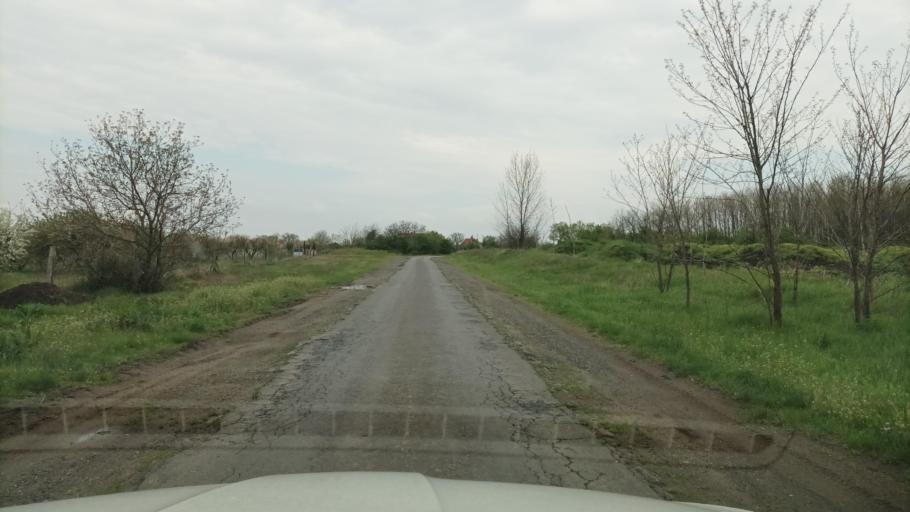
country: HU
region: Pest
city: Nagykoros
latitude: 47.0037
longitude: 19.7979
